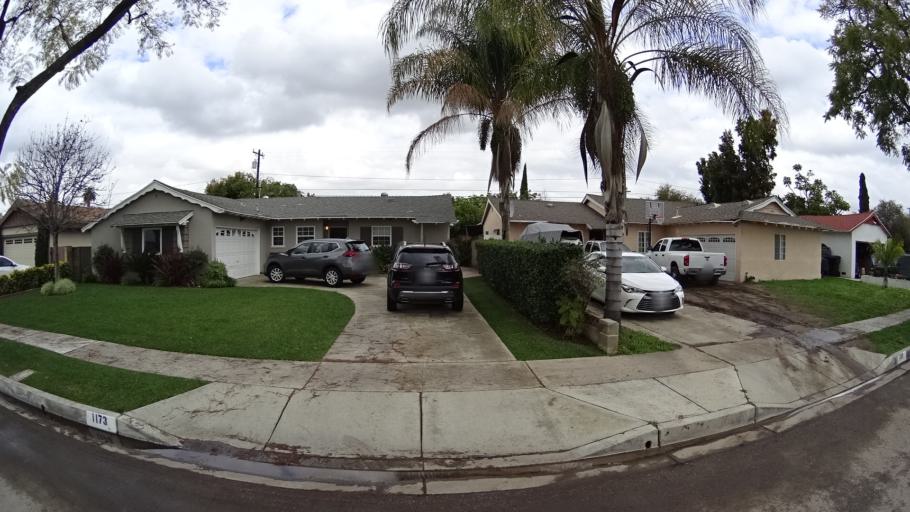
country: US
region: California
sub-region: Orange County
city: Anaheim
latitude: 33.8199
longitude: -117.9267
